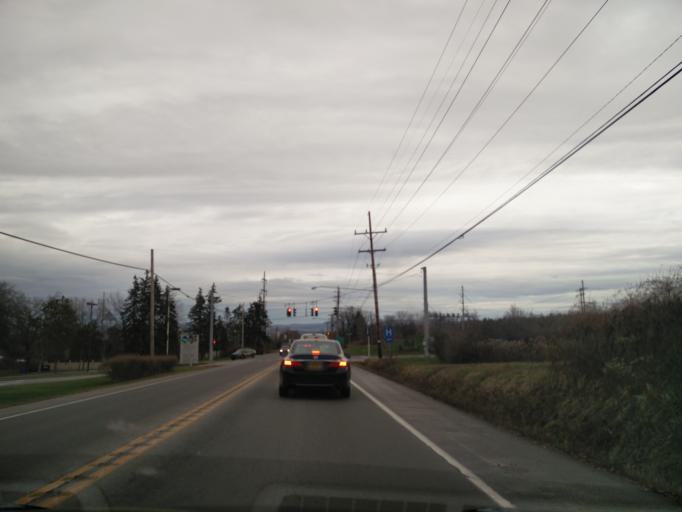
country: US
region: New York
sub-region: Tompkins County
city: Northwest Ithaca
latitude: 42.4669
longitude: -76.5402
